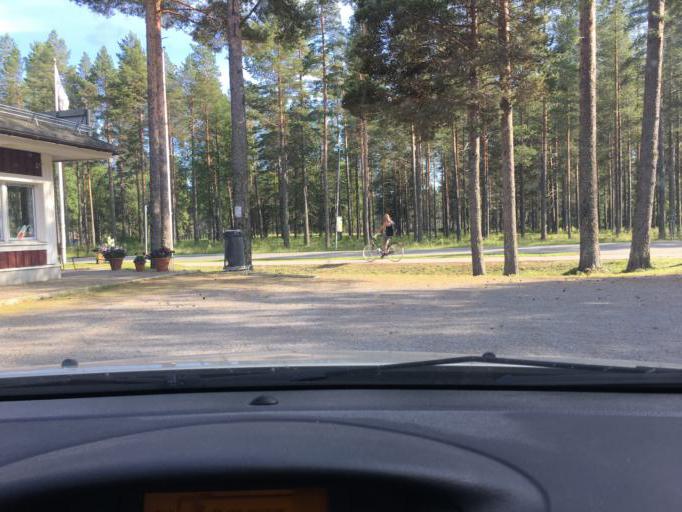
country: SE
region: Norrbotten
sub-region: Lulea Kommun
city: Bergnaset
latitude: 65.5966
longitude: 22.0679
